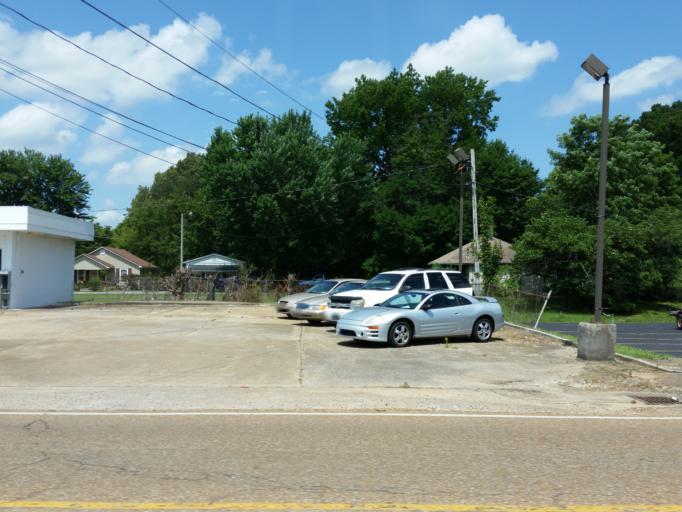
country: US
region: Tennessee
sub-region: Weakley County
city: Martin
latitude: 36.3484
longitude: -88.8495
